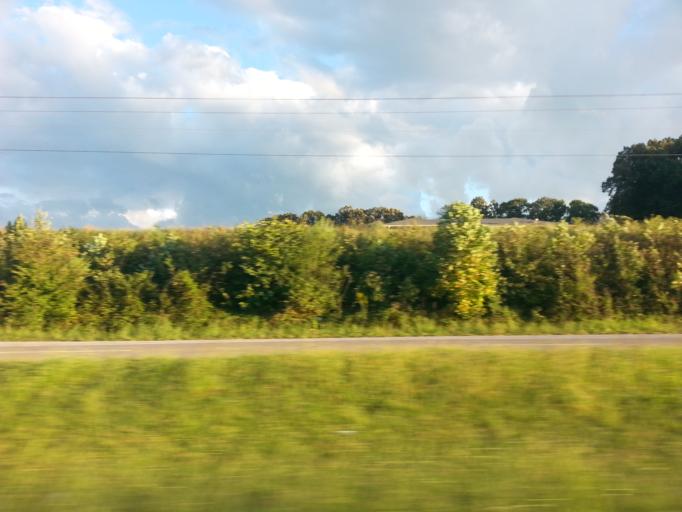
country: US
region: Tennessee
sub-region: Jefferson County
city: New Market
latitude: 36.0848
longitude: -83.6065
